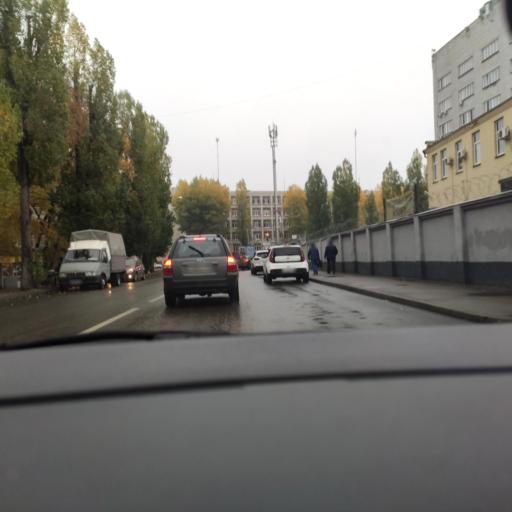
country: RU
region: Voronezj
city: Voronezh
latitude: 51.6798
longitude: 39.2585
